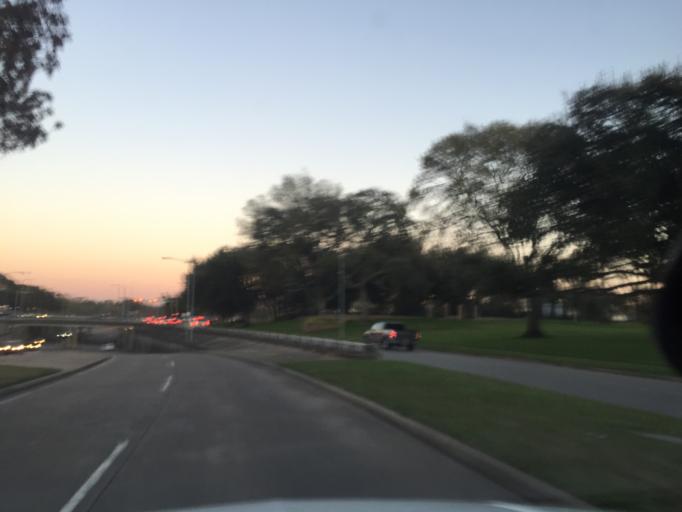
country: US
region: Texas
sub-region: Harris County
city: Houston
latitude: 29.7610
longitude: -95.3942
